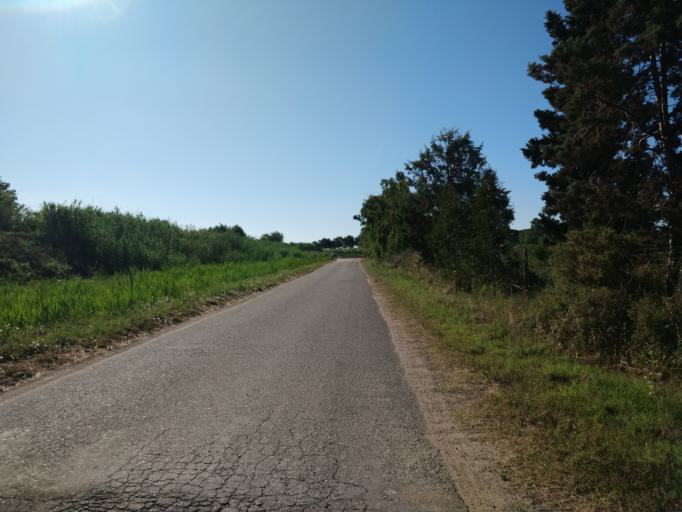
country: IT
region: Sardinia
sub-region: Provincia di Ogliastra
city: Lotzorai
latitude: 39.9601
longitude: 9.6806
